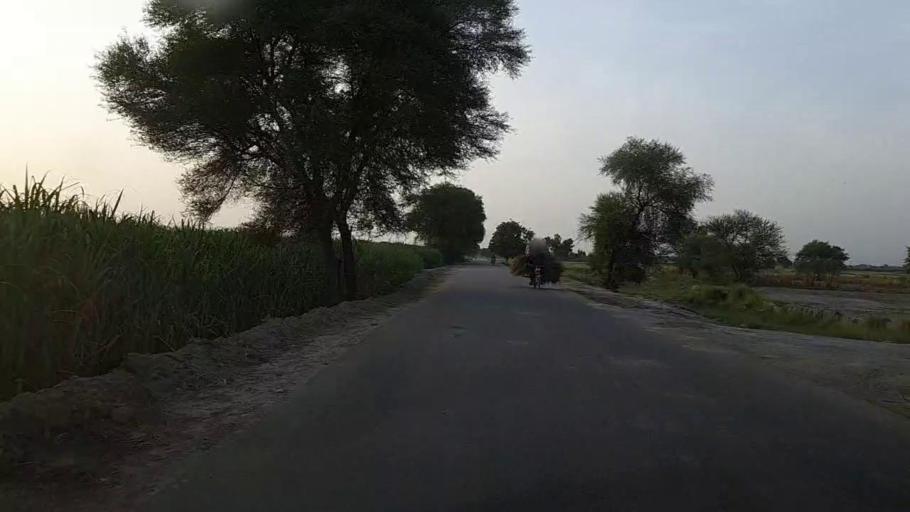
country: PK
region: Sindh
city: Ubauro
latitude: 28.2484
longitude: 69.8088
